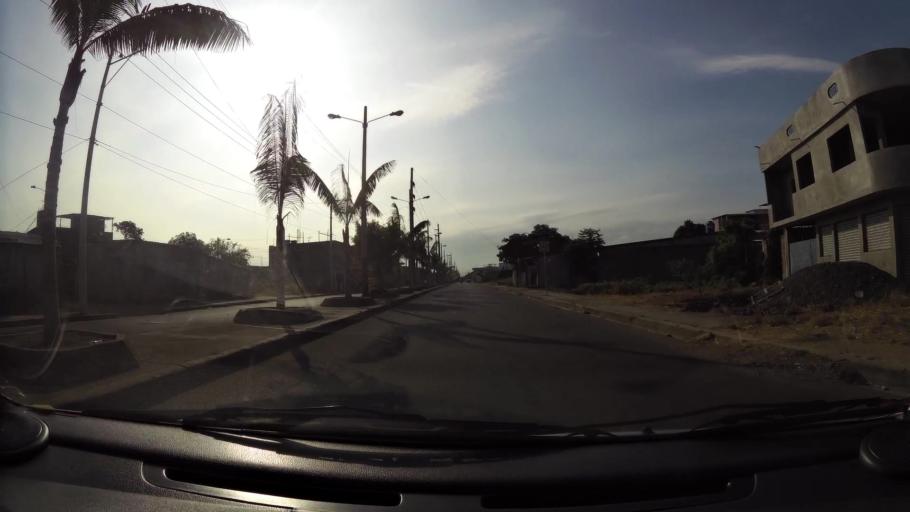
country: EC
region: Guayas
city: Eloy Alfaro
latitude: -2.1822
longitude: -79.8481
